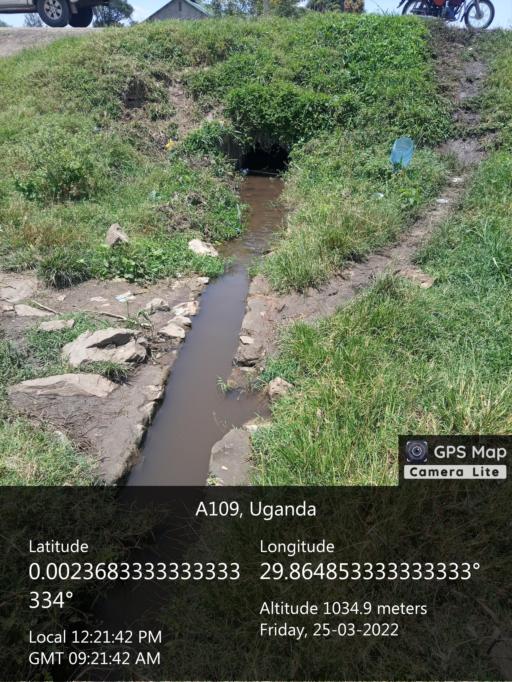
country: UG
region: Western Region
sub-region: Kasese District
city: Kilembe
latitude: 0.0024
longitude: 29.8649
